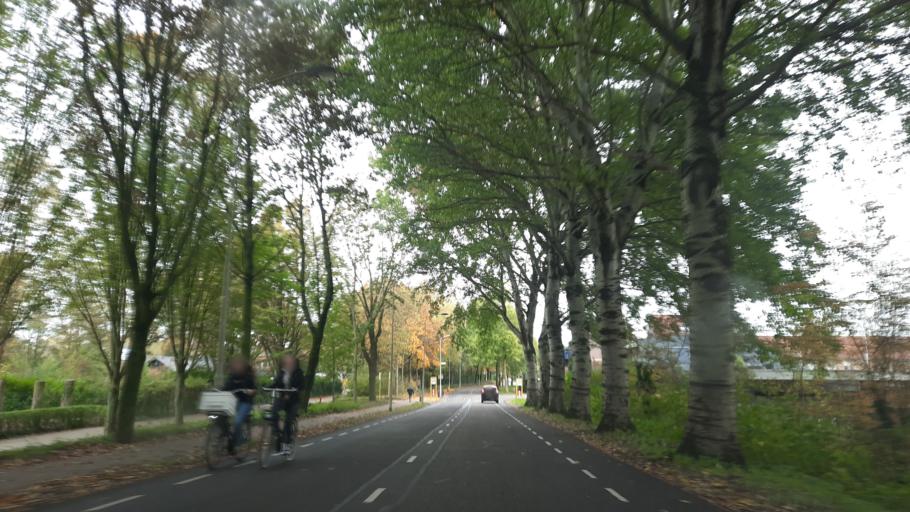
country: NL
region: South Holland
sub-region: Gemeente Gorinchem
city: Gorinchem
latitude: 51.8291
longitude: 4.9861
